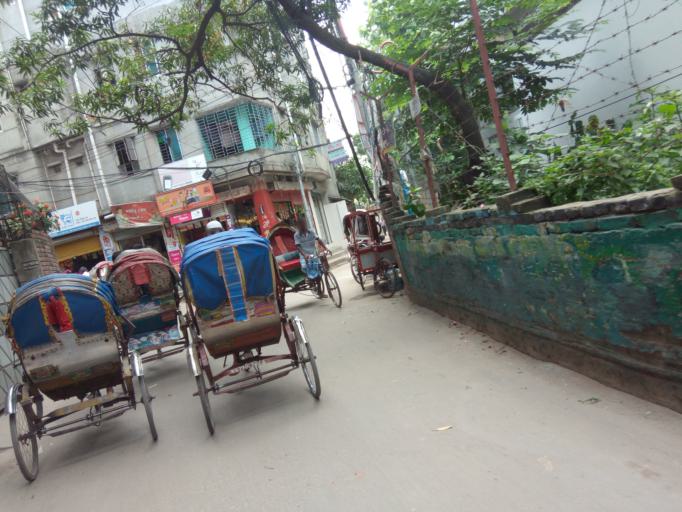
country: BD
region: Dhaka
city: Azimpur
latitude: 23.7523
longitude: 90.3898
